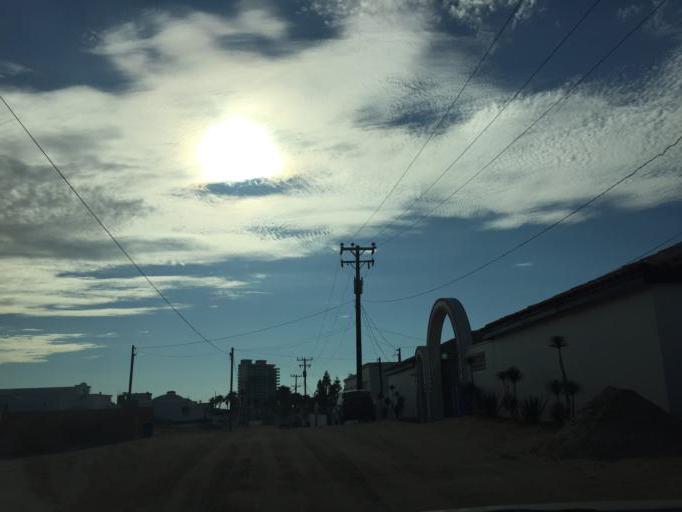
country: MX
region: Sonora
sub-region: Puerto Penasco
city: Puerto Penasco
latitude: 31.2828
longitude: -113.4543
